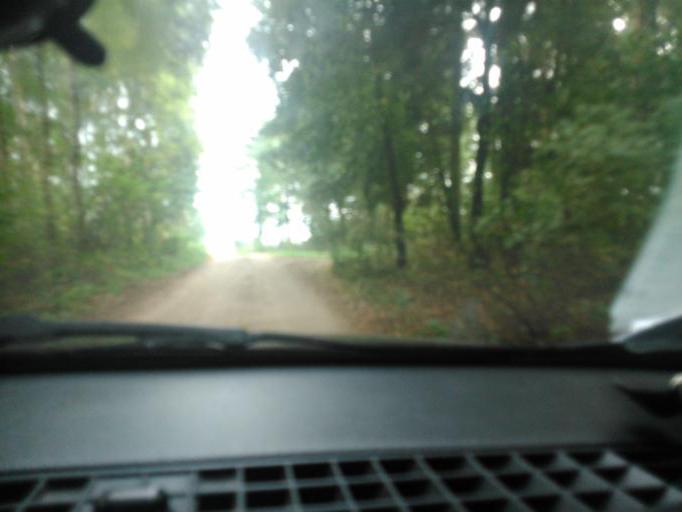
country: PL
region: Kujawsko-Pomorskie
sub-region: Powiat brodnicki
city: Swiedziebnia
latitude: 53.1861
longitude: 19.5369
